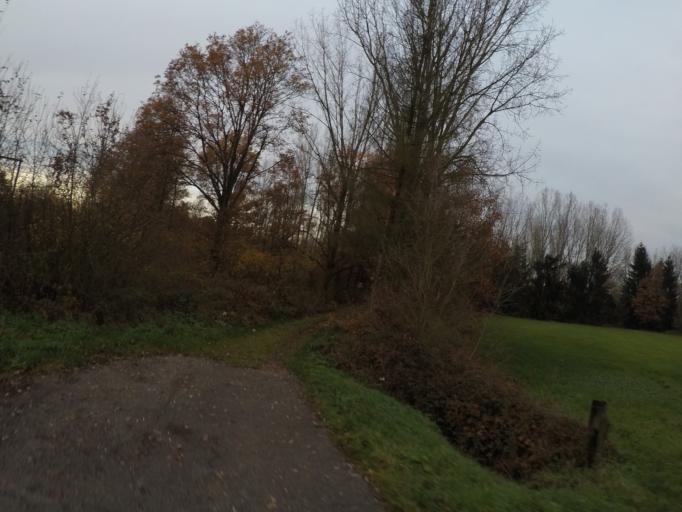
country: BE
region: Flanders
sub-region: Provincie Antwerpen
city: Lier
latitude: 51.1299
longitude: 4.6102
